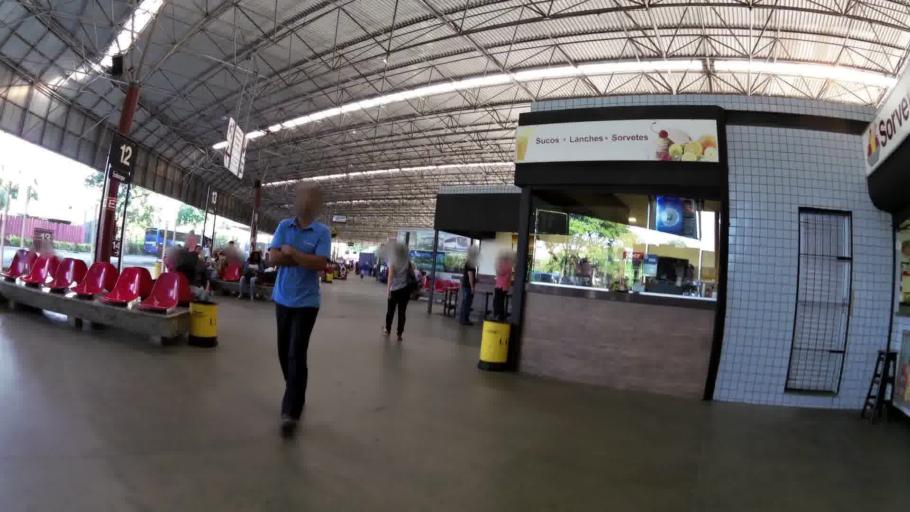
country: BR
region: Espirito Santo
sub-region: Vitoria
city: Vitoria
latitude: -20.3218
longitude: -40.3516
